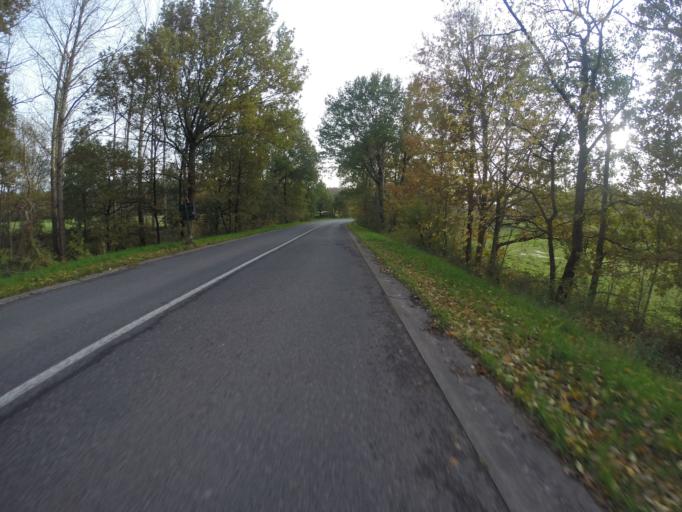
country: BE
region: Flanders
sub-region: Provincie Oost-Vlaanderen
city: Aalter
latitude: 51.0681
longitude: 3.4761
